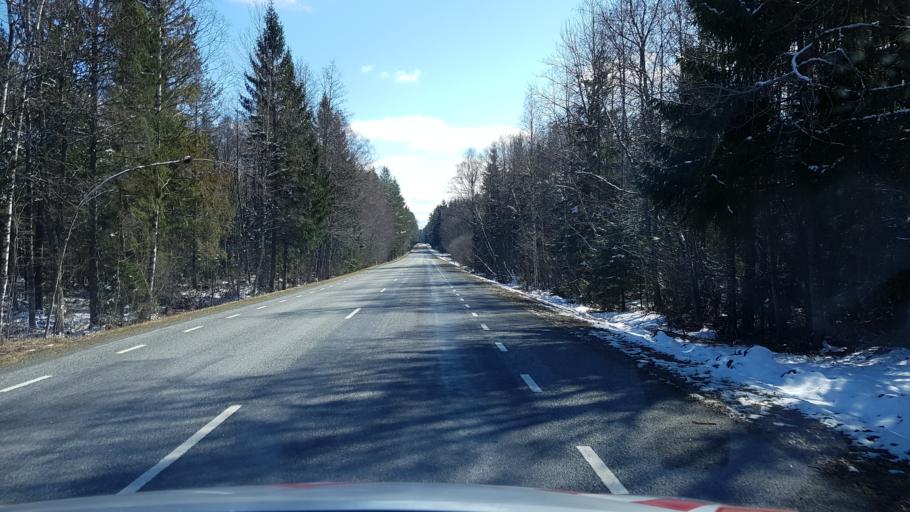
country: EE
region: Laeaene-Virumaa
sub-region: Tapa vald
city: Tapa
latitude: 59.4347
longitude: 25.9653
